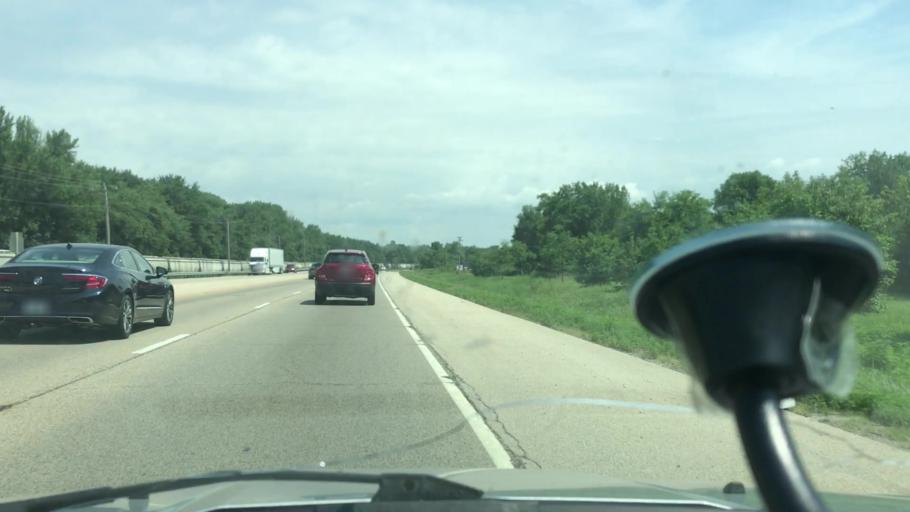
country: US
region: Illinois
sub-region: Tazewell County
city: North Pekin
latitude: 40.6064
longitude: -89.6358
